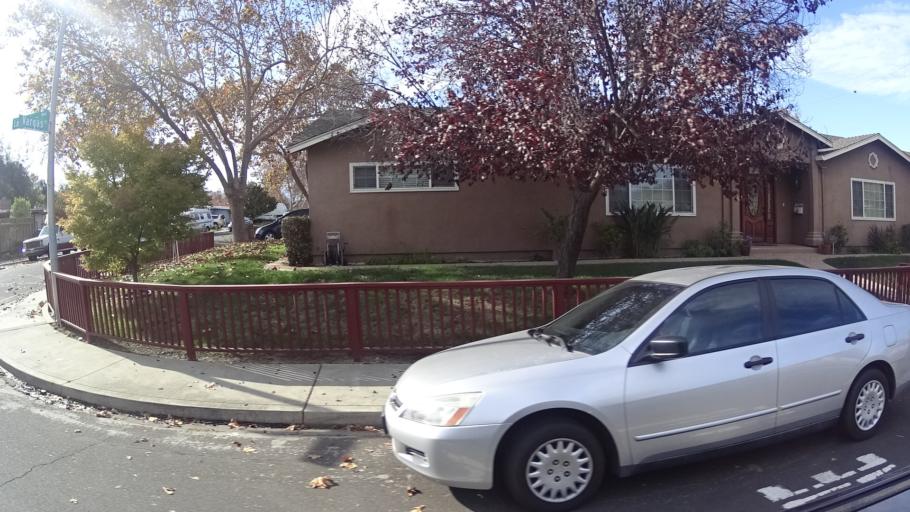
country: US
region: California
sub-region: Santa Clara County
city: Santa Clara
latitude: 37.3573
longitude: -121.9650
